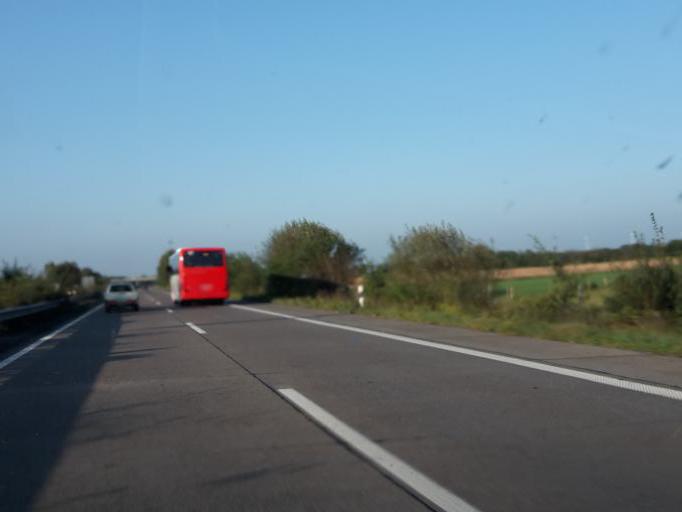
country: DE
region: Lower Saxony
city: Grossenkneten
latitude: 52.9563
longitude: 8.1817
